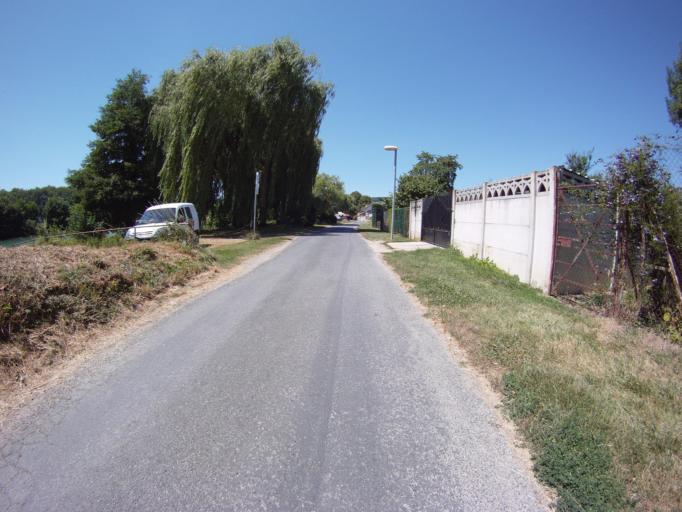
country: FR
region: Champagne-Ardenne
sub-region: Departement de la Marne
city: Damery
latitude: 49.0682
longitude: 3.8807
